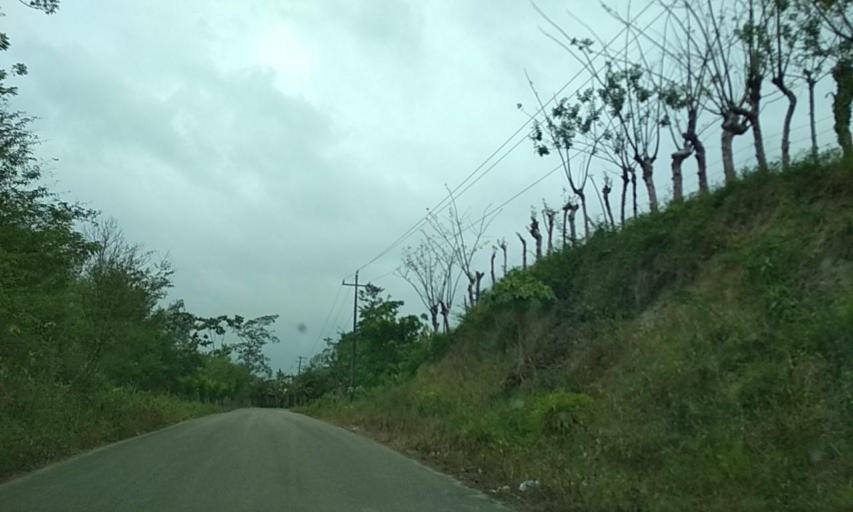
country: MX
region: Tabasco
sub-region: Huimanguillo
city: Francisco Rueda
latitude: 17.6033
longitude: -94.0923
